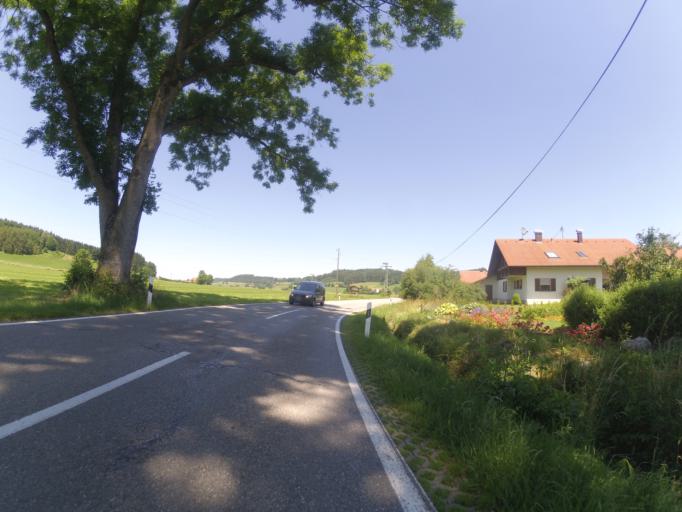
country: DE
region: Bavaria
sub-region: Swabia
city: Untrasried
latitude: 47.8564
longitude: 10.3542
